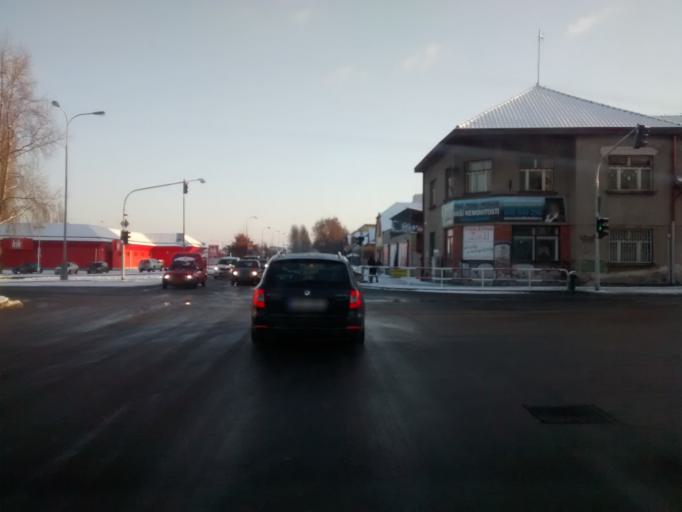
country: CZ
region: Central Bohemia
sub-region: Okres Melnik
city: Melnik
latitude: 50.3495
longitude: 14.4881
